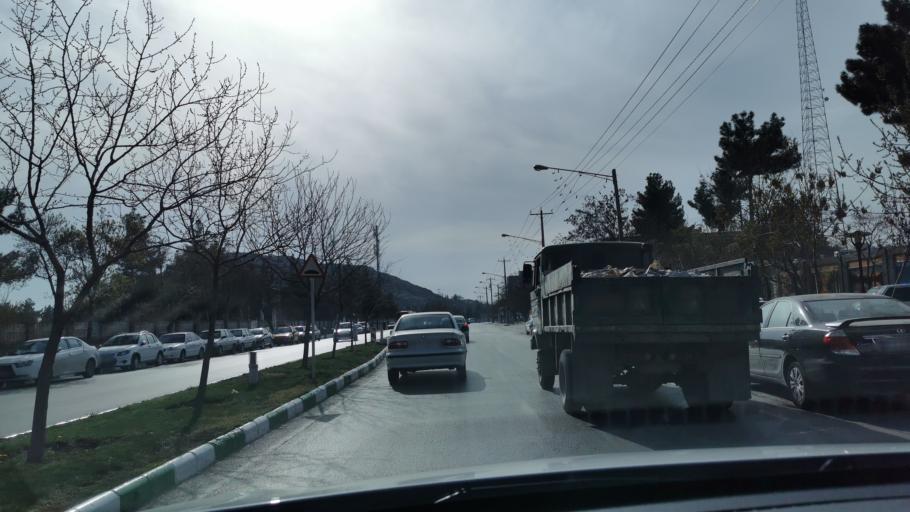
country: IR
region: Razavi Khorasan
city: Mashhad
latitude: 36.2817
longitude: 59.5526
